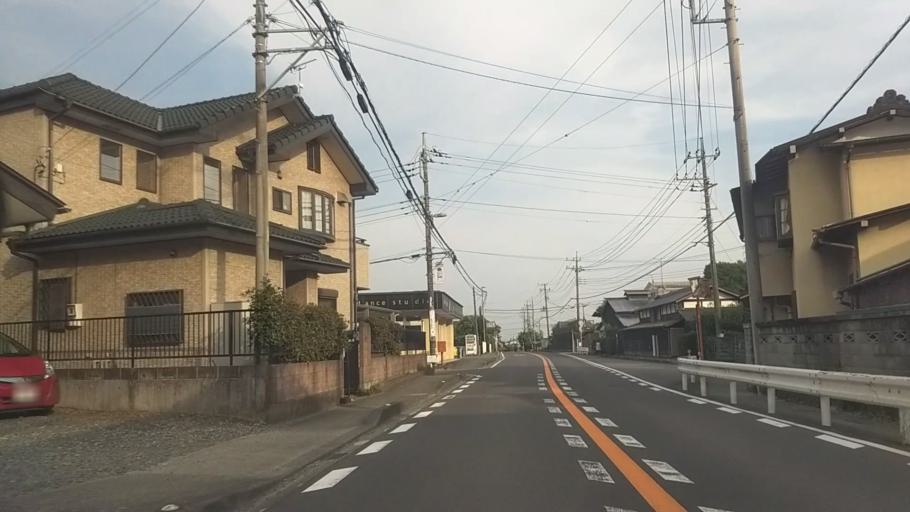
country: JP
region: Kanagawa
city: Odawara
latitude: 35.3549
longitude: 139.0909
